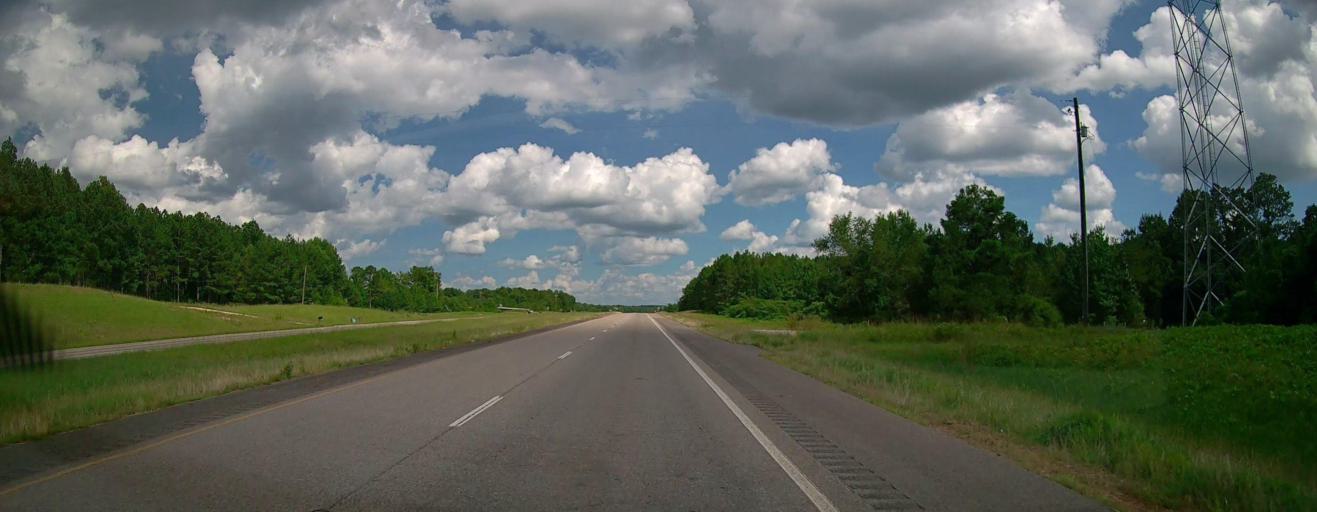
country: US
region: Mississippi
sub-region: Lowndes County
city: New Hope
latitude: 33.4746
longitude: -88.2471
